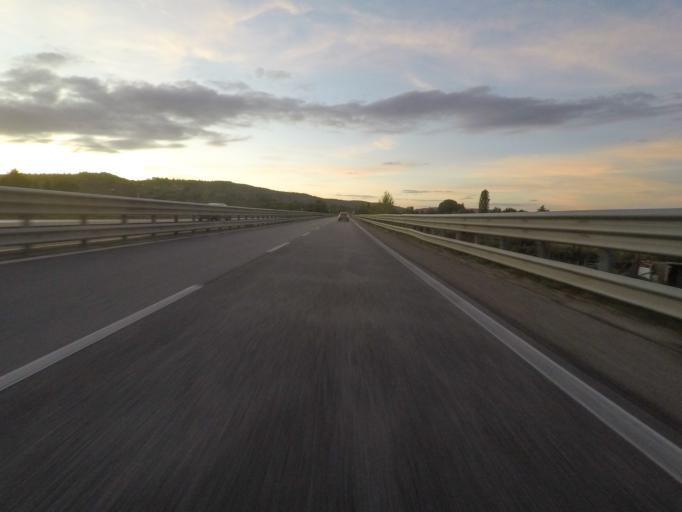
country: IT
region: Tuscany
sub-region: Provincia di Siena
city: Sinalunga
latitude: 43.2276
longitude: 11.7363
